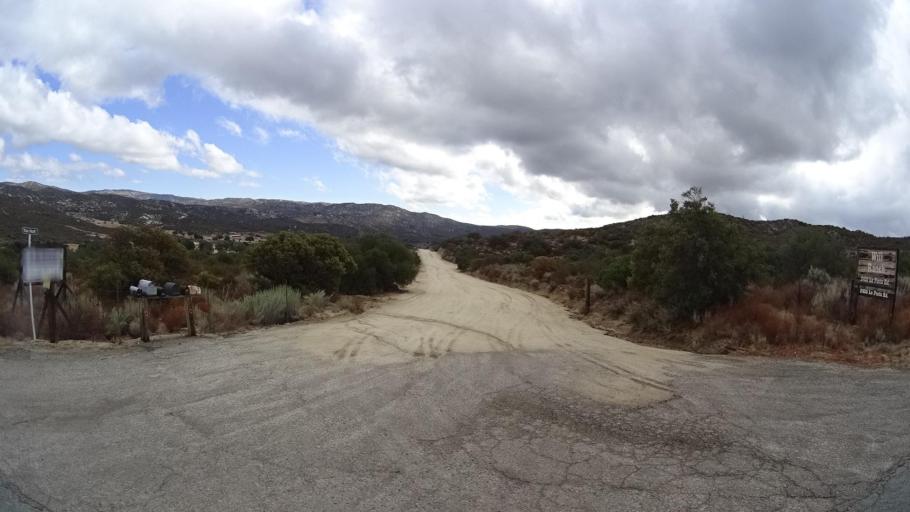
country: US
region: California
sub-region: San Diego County
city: Campo
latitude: 32.6781
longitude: -116.4288
